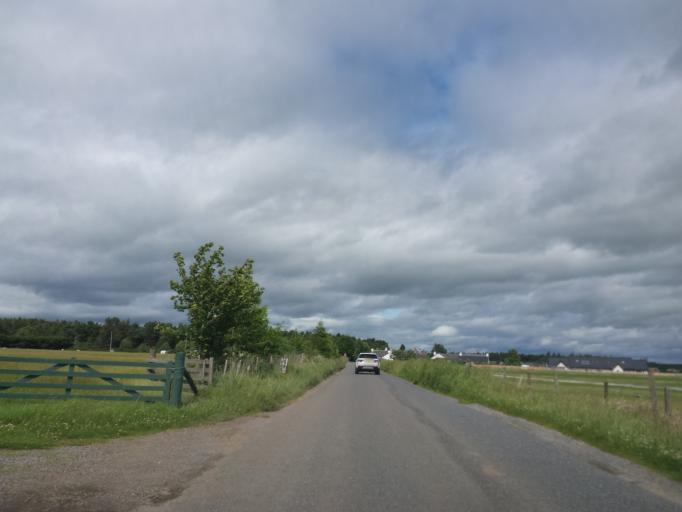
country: GB
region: Scotland
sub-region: Highland
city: Fortrose
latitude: 57.4770
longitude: -4.0863
